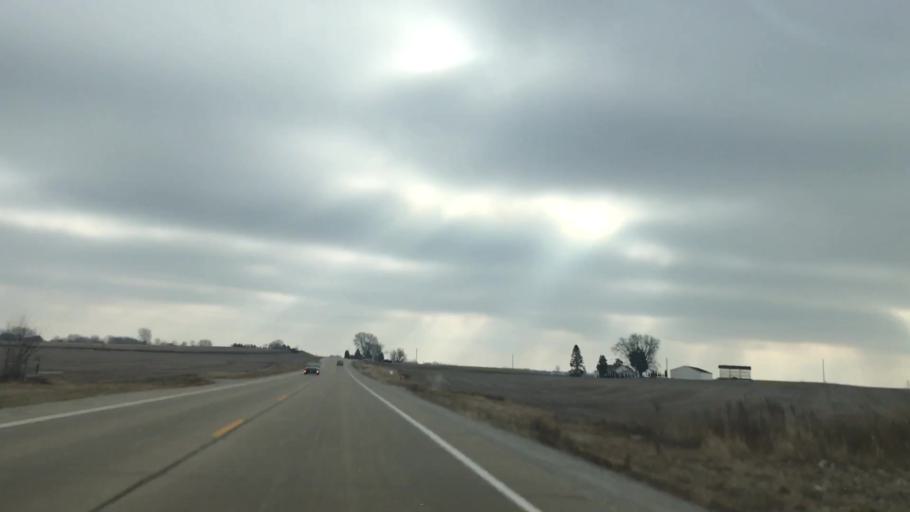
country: US
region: Wisconsin
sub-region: Dodge County
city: Beaver Dam
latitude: 43.4808
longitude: -88.7841
